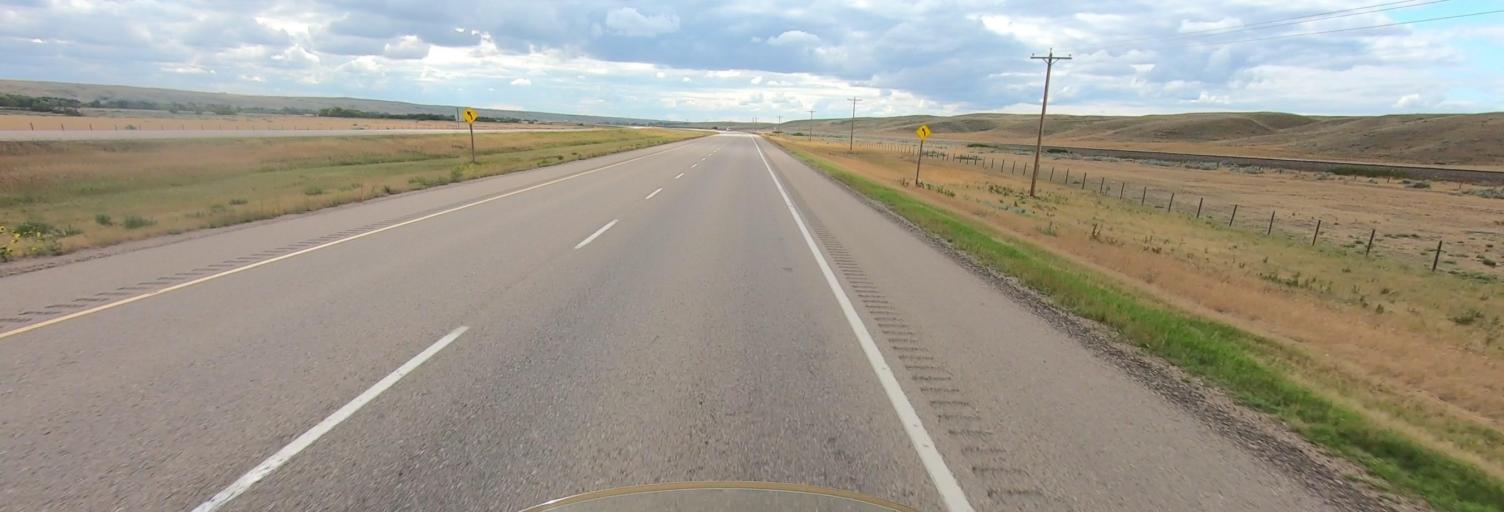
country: CA
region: Alberta
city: Medicine Hat
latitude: 49.9573
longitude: -110.2926
